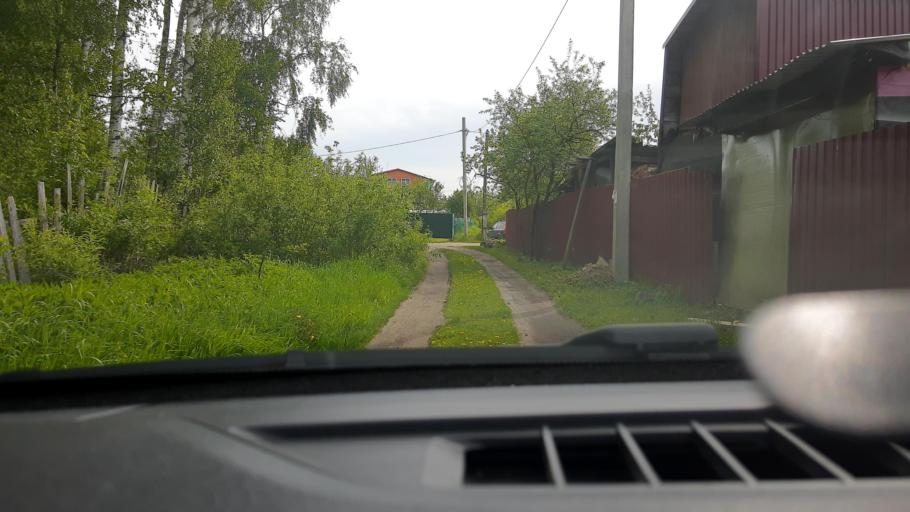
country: RU
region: Nizjnij Novgorod
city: Gorbatovka
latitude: 56.3048
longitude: 43.7653
